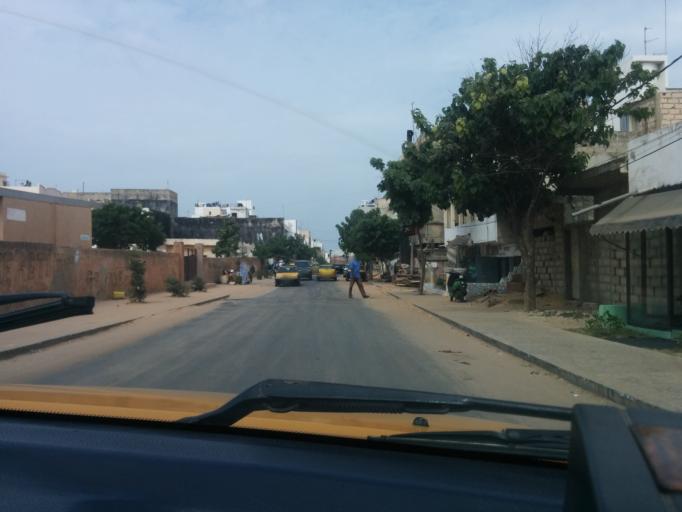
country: SN
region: Dakar
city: Grand Dakar
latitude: 14.7515
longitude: -17.4533
